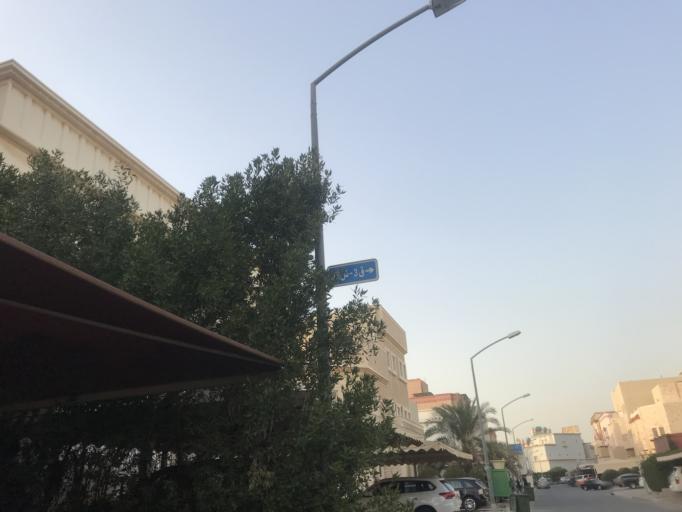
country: KW
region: Al Asimah
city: Ar Rabiyah
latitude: 29.2446
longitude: 47.9054
